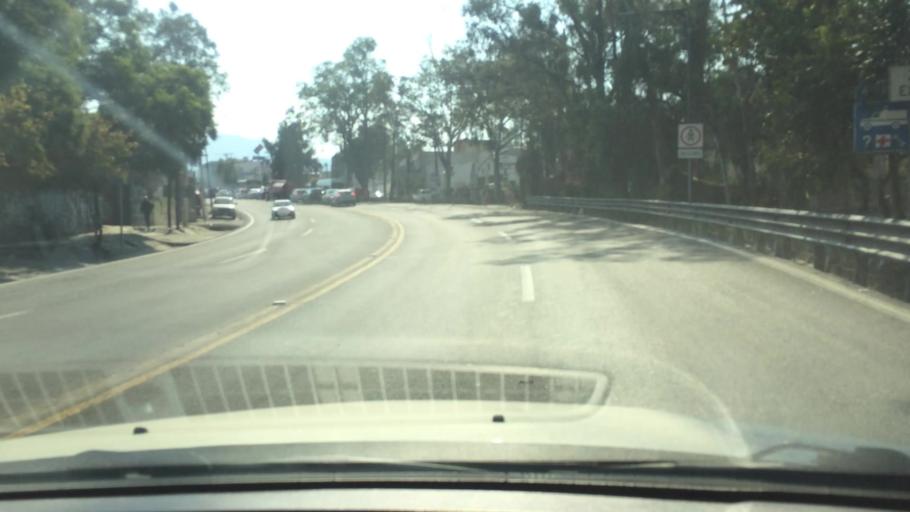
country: MX
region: Mexico City
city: Tlalpan
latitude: 19.2705
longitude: -99.1702
